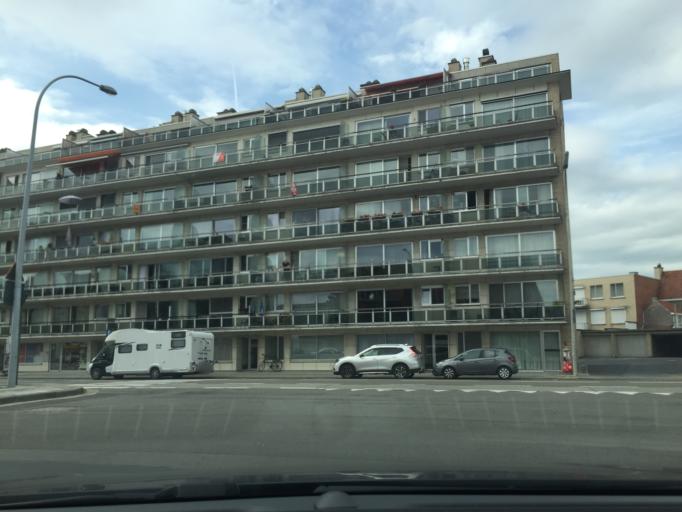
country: BE
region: Flanders
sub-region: Provincie West-Vlaanderen
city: Roeselare
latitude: 50.9409
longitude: 3.1304
